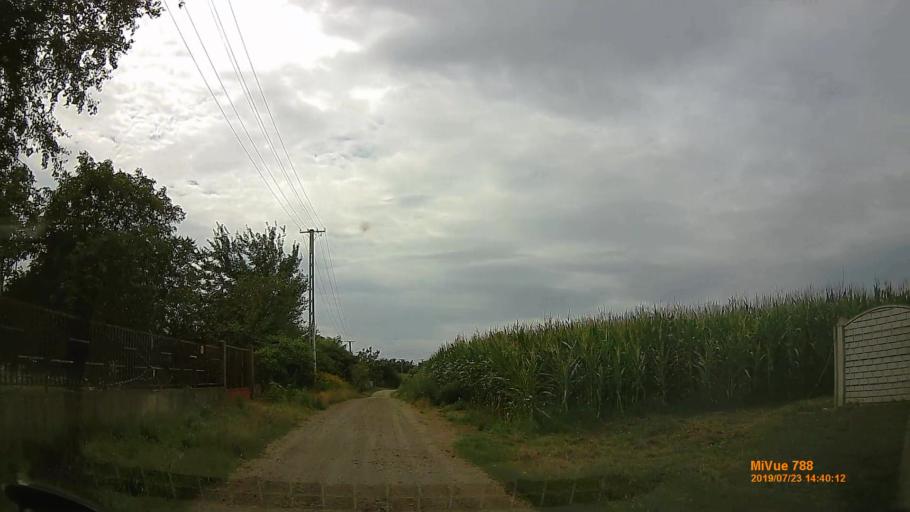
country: HU
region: Szabolcs-Szatmar-Bereg
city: Kalmanhaza
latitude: 47.9212
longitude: 21.6486
